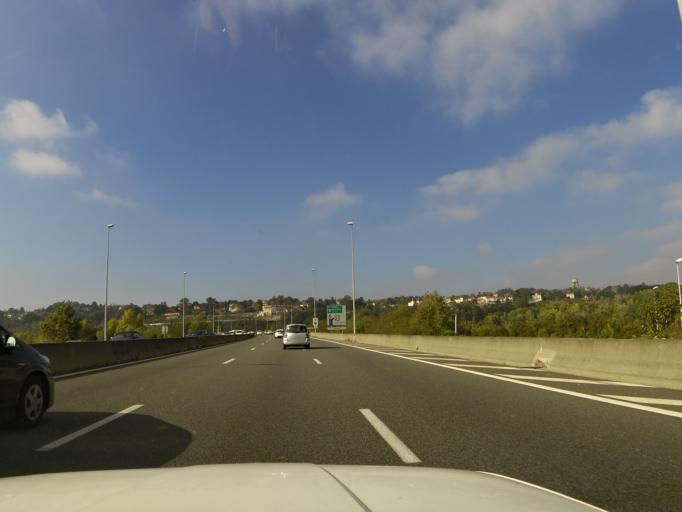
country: FR
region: Rhone-Alpes
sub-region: Departement du Rhone
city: Villeurbanne
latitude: 45.7916
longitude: 4.8830
